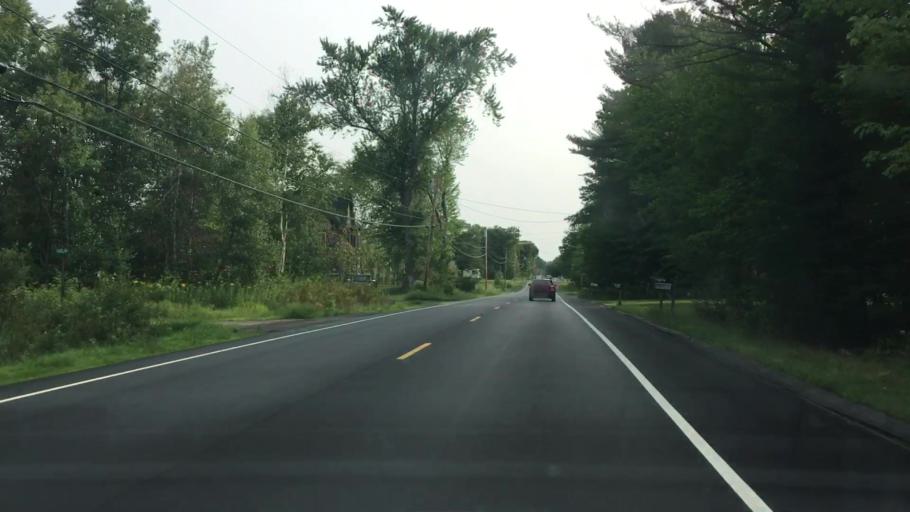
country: US
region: Maine
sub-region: Kennebec County
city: Chelsea
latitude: 44.2610
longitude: -69.7060
